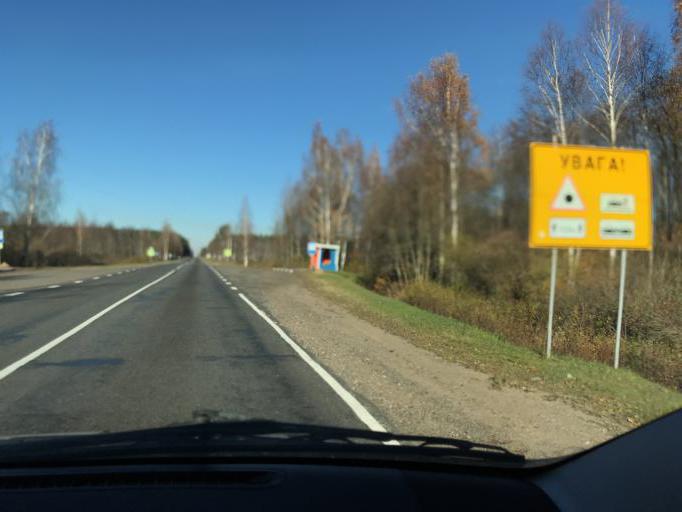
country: BY
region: Vitebsk
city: Polatsk
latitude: 55.4304
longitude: 28.7838
